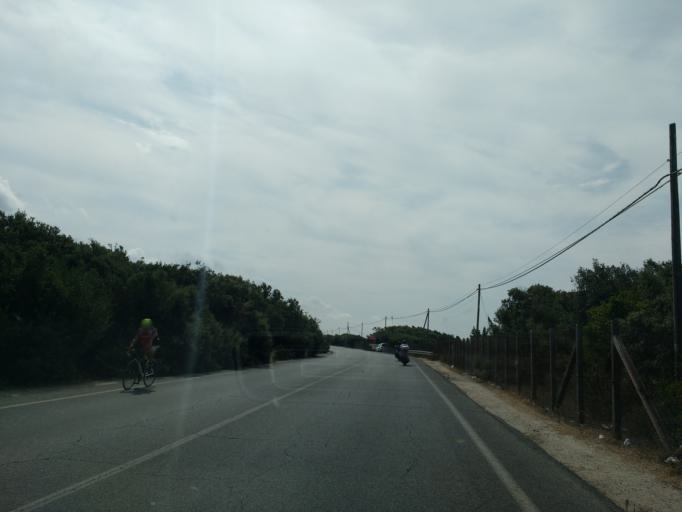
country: IT
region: Latium
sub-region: Citta metropolitana di Roma Capitale
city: Torvaianica
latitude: 41.6847
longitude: 12.3782
